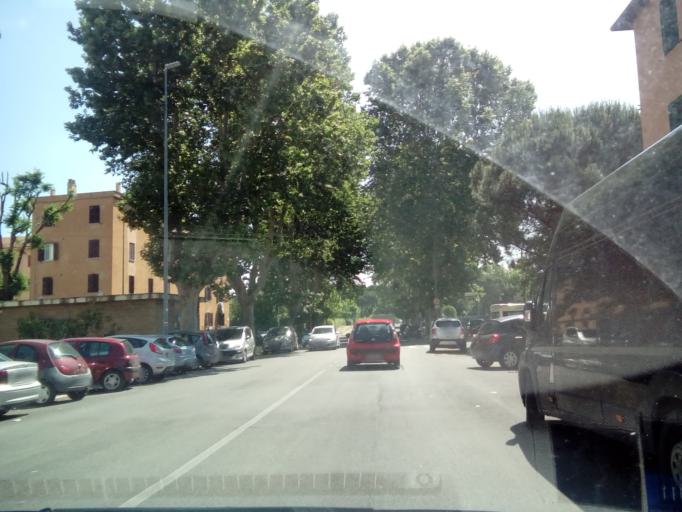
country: IT
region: Latium
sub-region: Citta metropolitana di Roma Capitale
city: Rome
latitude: 41.8900
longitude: 12.5769
